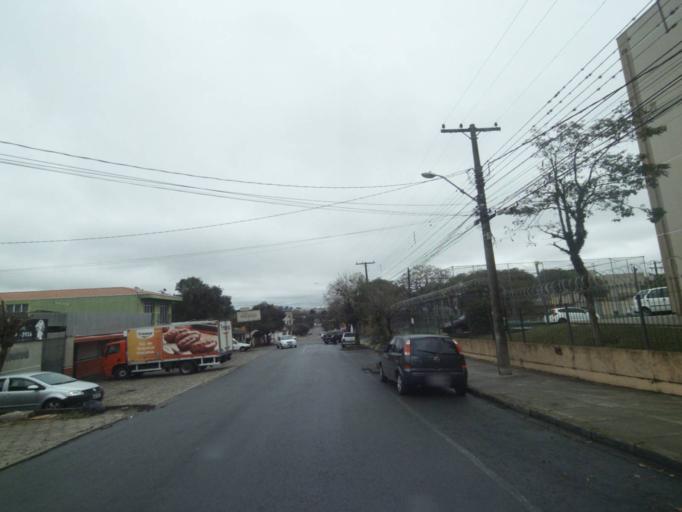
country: BR
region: Parana
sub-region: Curitiba
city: Curitiba
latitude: -25.5059
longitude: -49.2986
